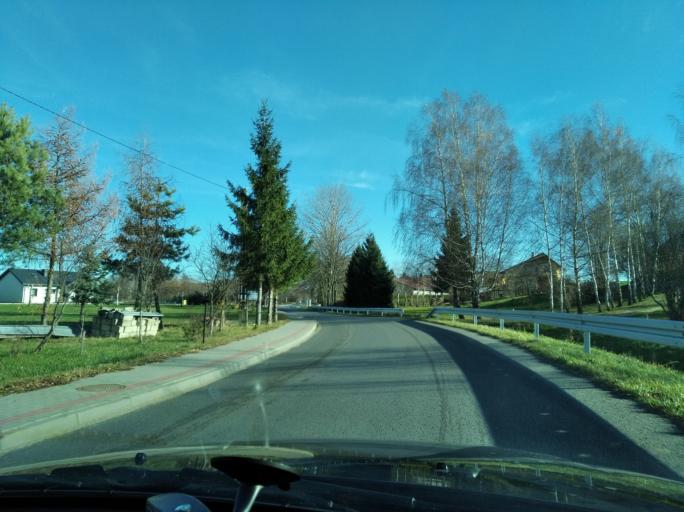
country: PL
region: Subcarpathian Voivodeship
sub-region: Powiat rzeszowski
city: Lutoryz
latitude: 49.9806
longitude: 21.9149
